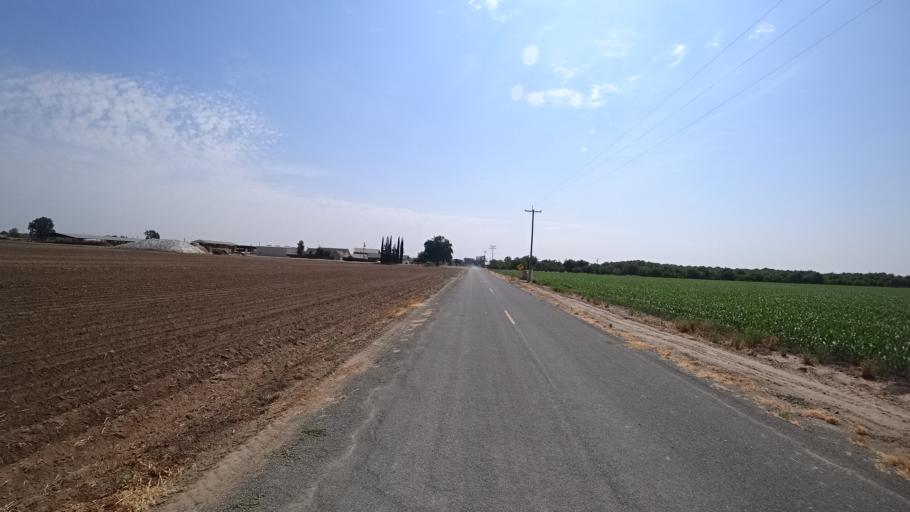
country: US
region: California
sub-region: Fresno County
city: Riverdale
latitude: 36.3948
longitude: -119.7842
